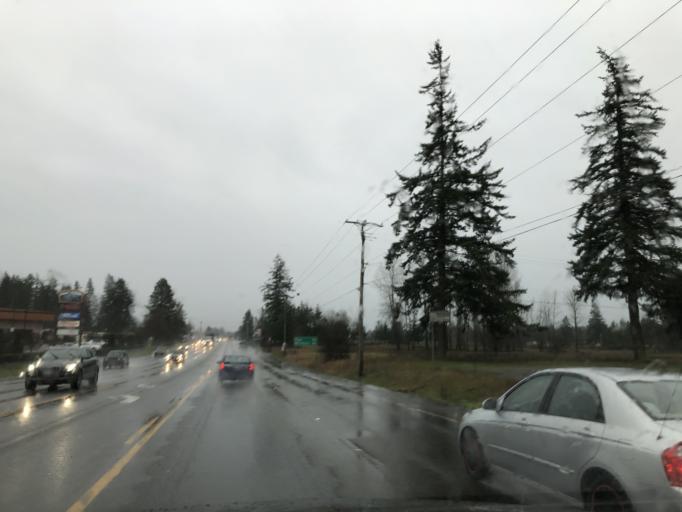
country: US
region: Washington
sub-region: Pierce County
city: Spanaway
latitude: 47.0817
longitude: -122.4326
